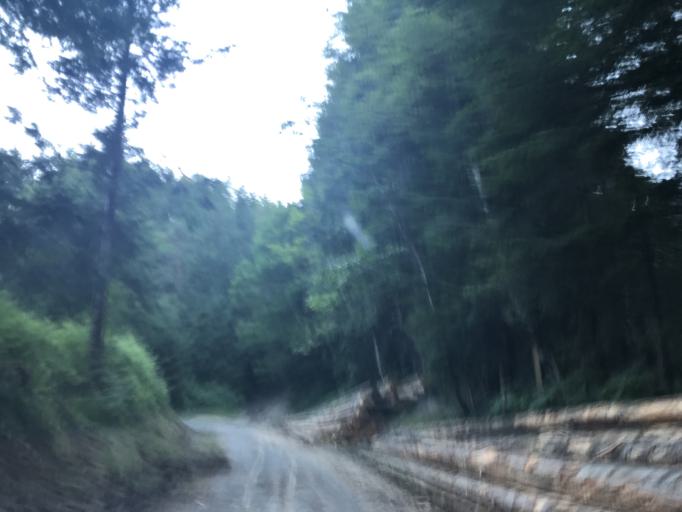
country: FR
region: Auvergne
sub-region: Departement du Puy-de-Dome
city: Celles-sur-Durolle
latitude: 45.7911
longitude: 3.6808
